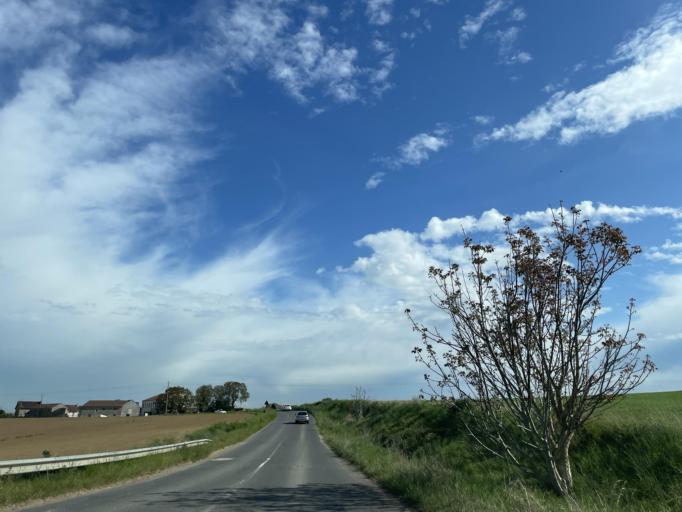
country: FR
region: Ile-de-France
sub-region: Departement de Seine-et-Marne
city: Charny
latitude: 48.9497
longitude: 2.7733
